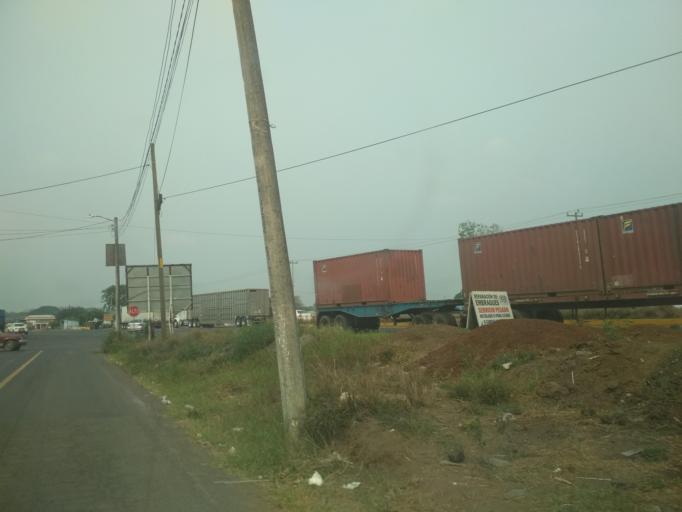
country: MX
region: Veracruz
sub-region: Veracruz
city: Delfino Victoria (Santa Fe)
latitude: 19.2220
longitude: -96.2580
